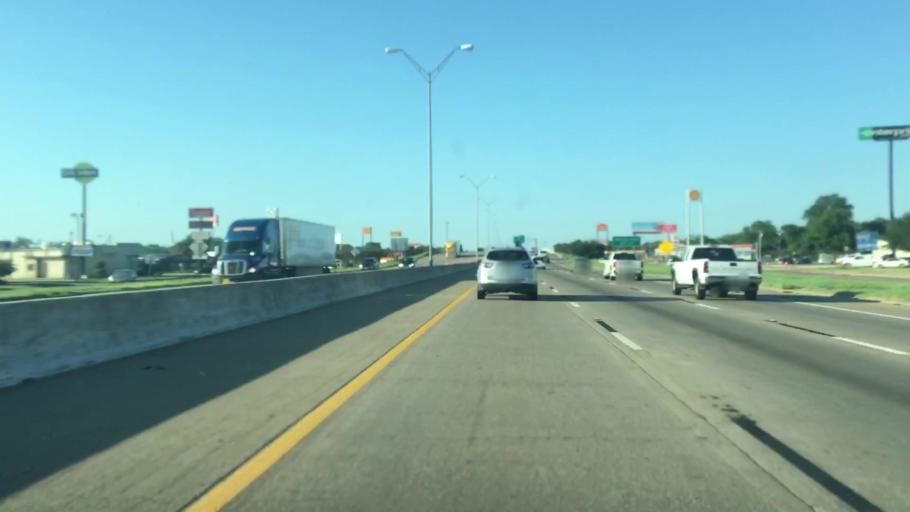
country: US
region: Texas
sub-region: McLennan County
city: Beverly
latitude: 31.5386
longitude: -97.1288
